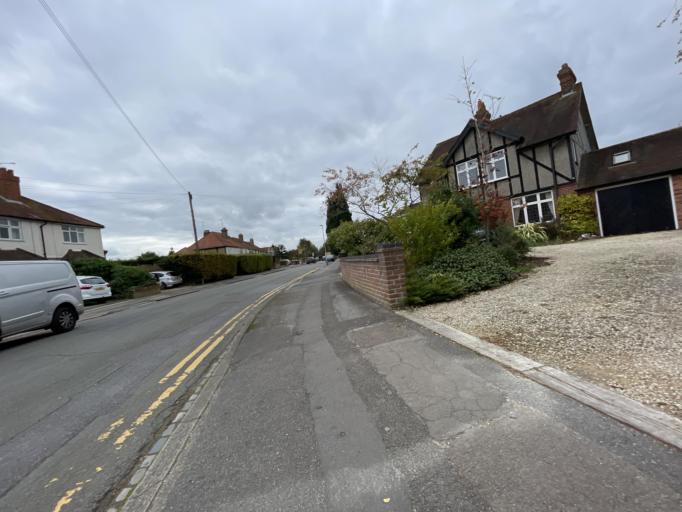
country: GB
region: England
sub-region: West Berkshire
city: Tilehurst
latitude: 51.4565
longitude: -1.0270
